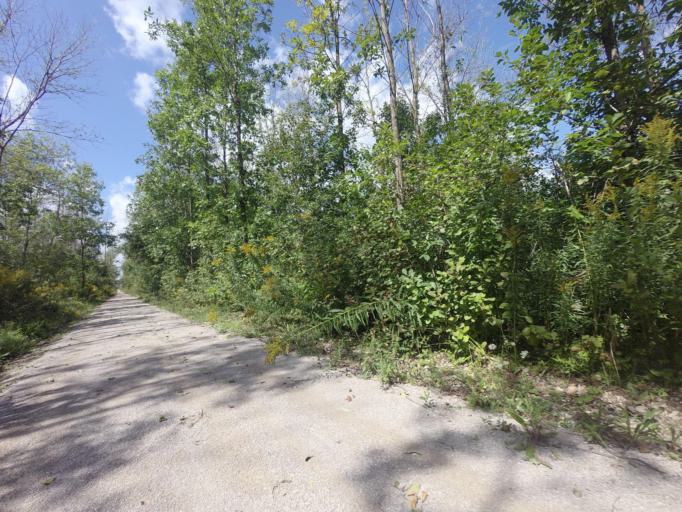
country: CA
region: Ontario
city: Huron East
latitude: 43.6187
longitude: -81.1504
